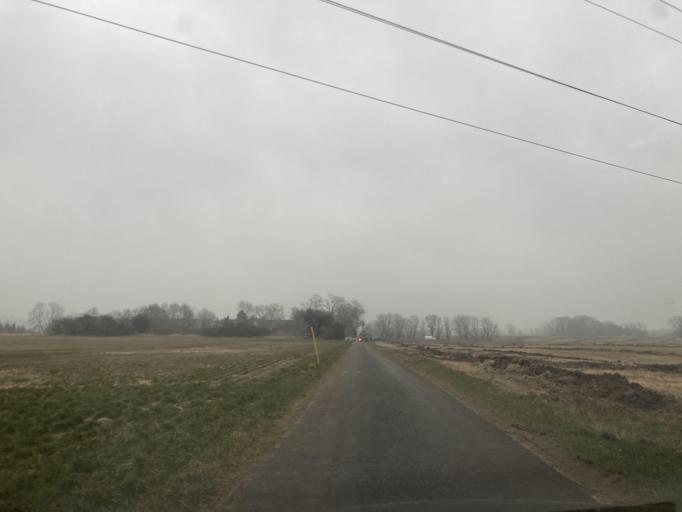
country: DK
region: Zealand
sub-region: Vordingborg Kommune
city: Neder Vindinge
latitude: 55.1556
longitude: 11.9020
